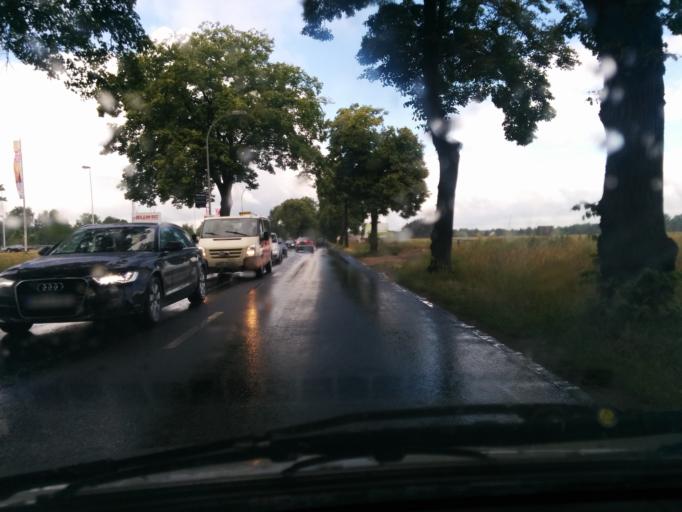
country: DE
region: Brandenburg
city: Falkensee
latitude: 52.5611
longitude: 13.1248
